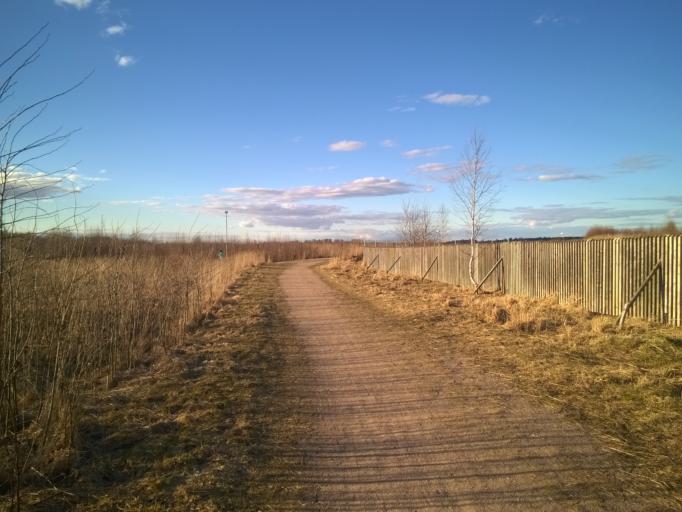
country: FI
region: Uusimaa
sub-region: Helsinki
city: Vantaa
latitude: 60.2459
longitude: 25.0415
